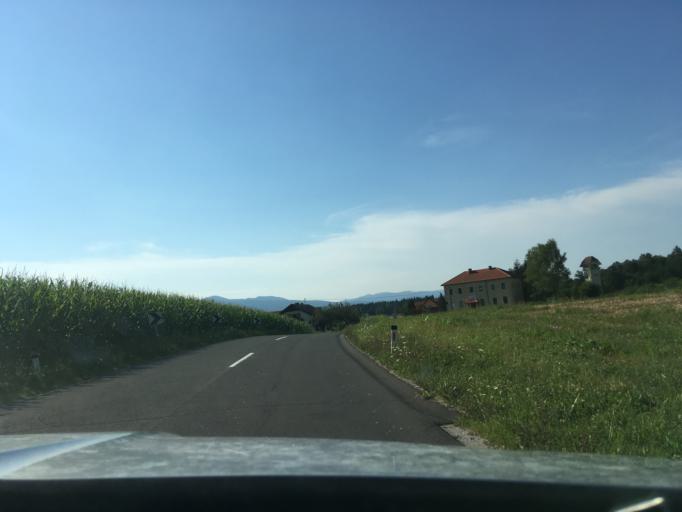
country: SI
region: Crnomelj
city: Crnomelj
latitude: 45.4779
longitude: 15.2095
